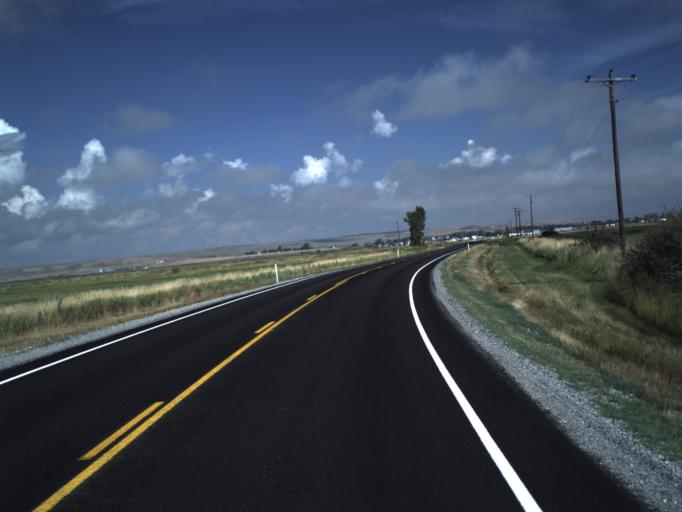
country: US
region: Utah
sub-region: Rich County
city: Randolph
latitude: 41.6413
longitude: -111.1830
